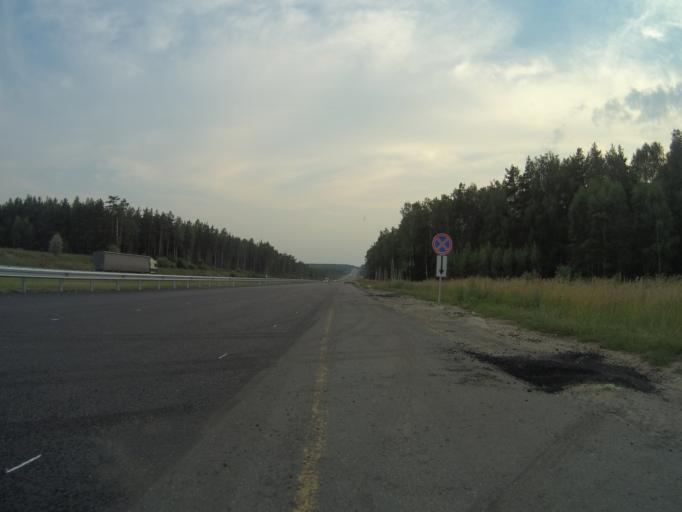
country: RU
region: Vladimir
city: Sudogda
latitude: 56.1315
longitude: 40.8788
